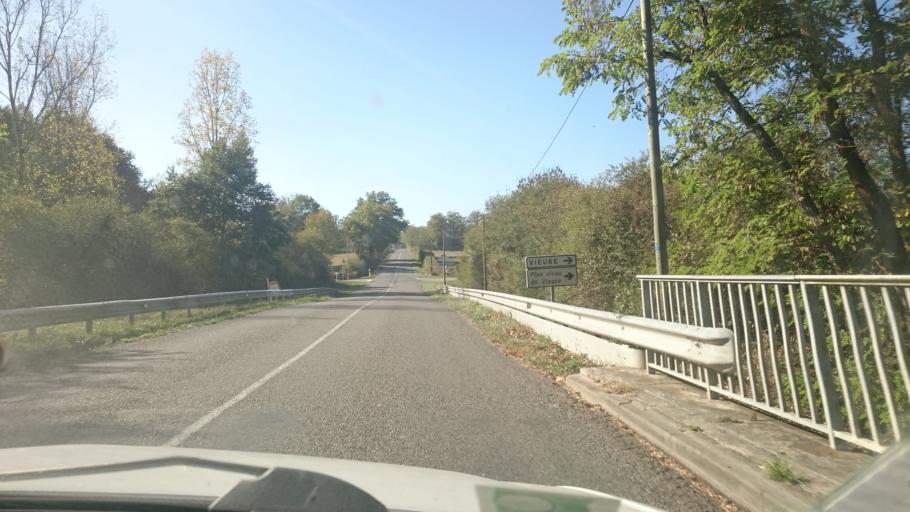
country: FR
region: Auvergne
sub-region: Departement de l'Allier
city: Buxieres-les-Mines
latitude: 46.4973
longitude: 2.9145
